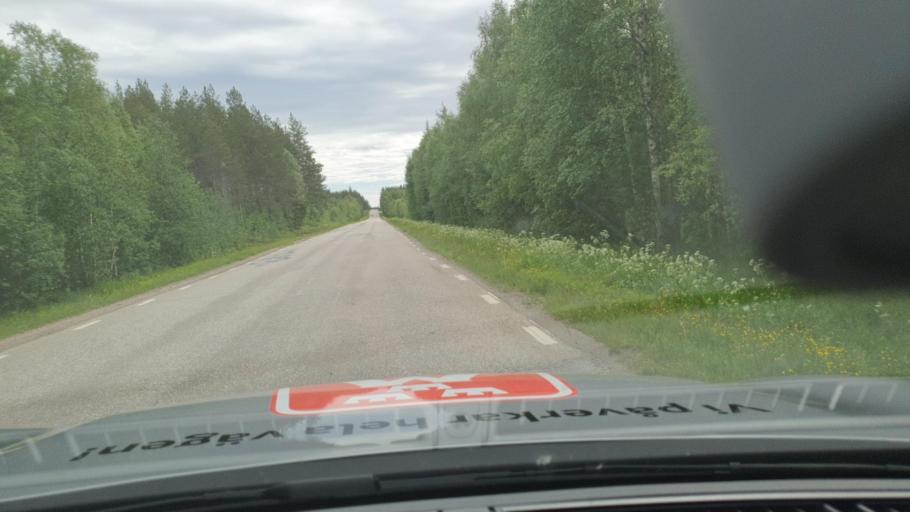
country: SE
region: Norrbotten
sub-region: Kalix Kommun
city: Kalix
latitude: 65.9177
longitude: 23.1728
